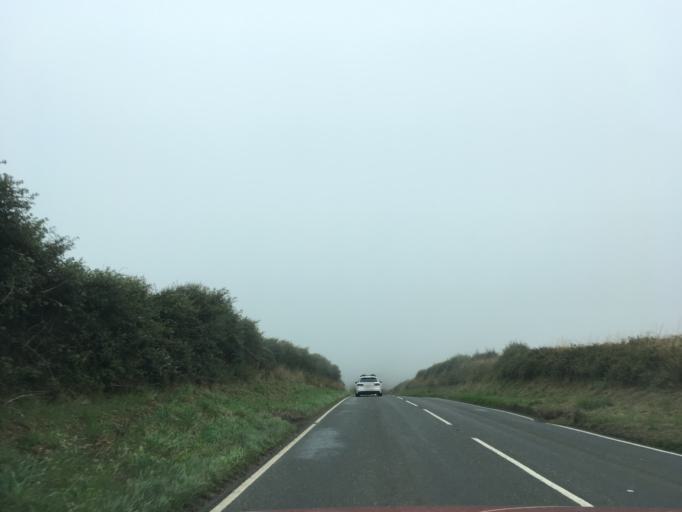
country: GB
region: Wales
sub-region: Pembrokeshire
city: Llanrhian
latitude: 51.8719
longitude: -5.1537
